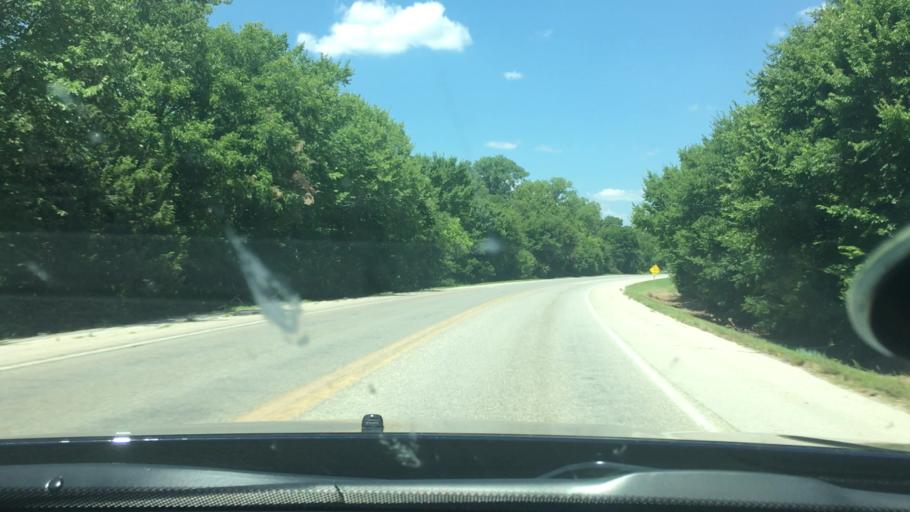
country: US
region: Oklahoma
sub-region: Marshall County
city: Oakland
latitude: 34.1740
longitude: -96.8550
